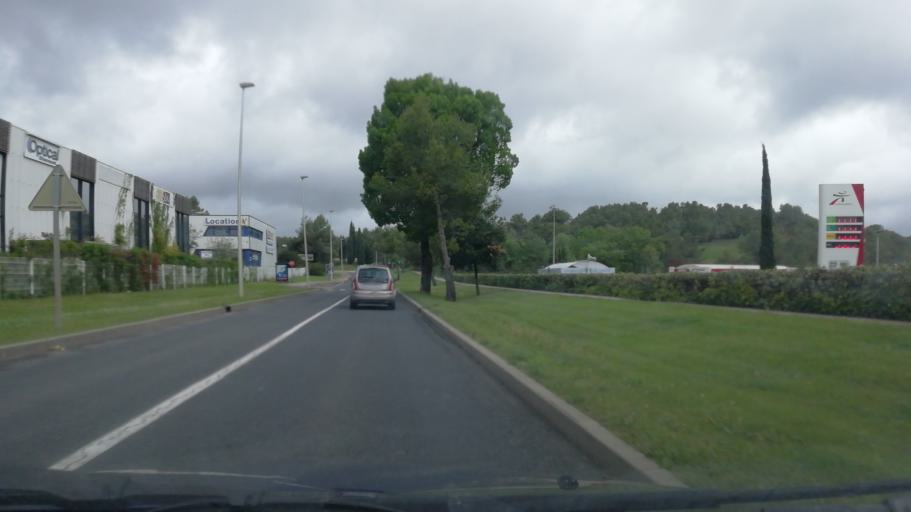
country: FR
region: Languedoc-Roussillon
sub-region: Departement de l'Herault
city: Saint-Clement-de-Riviere
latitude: 43.6770
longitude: 3.8173
